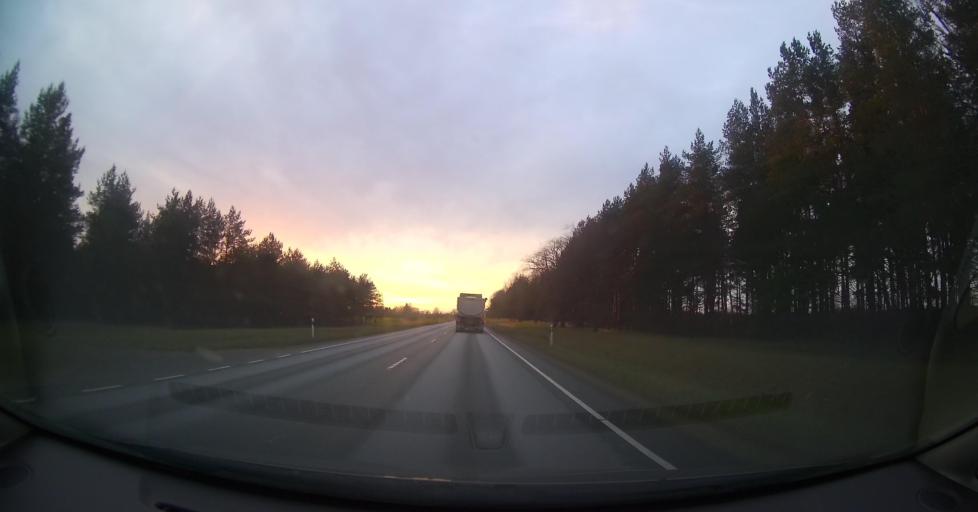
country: EE
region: Ida-Virumaa
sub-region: Aseri vald
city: Aseri
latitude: 59.4369
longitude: 26.7209
